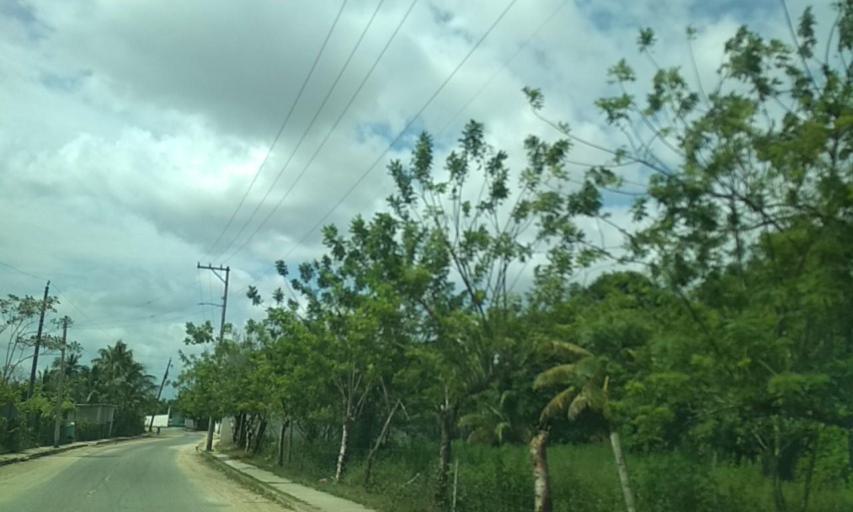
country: MX
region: Veracruz
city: Las Choapas
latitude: 17.8902
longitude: -94.1087
